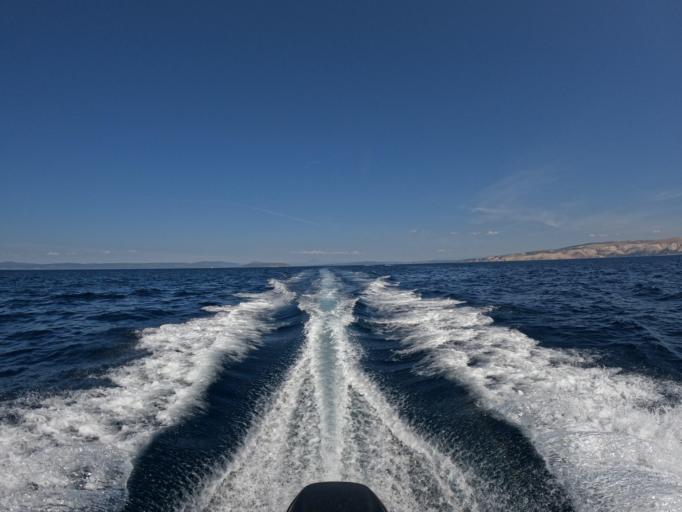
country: HR
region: Primorsko-Goranska
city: Lopar
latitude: 44.8926
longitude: 14.6431
